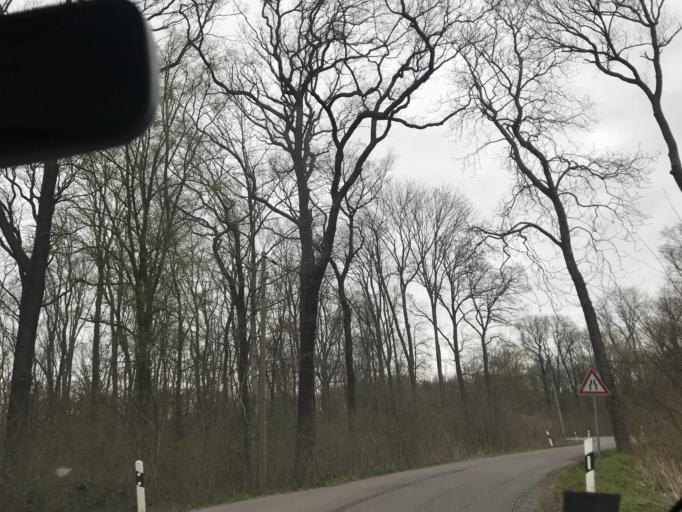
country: DE
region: Saxony
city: Schkeuditz
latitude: 51.3667
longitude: 12.2552
